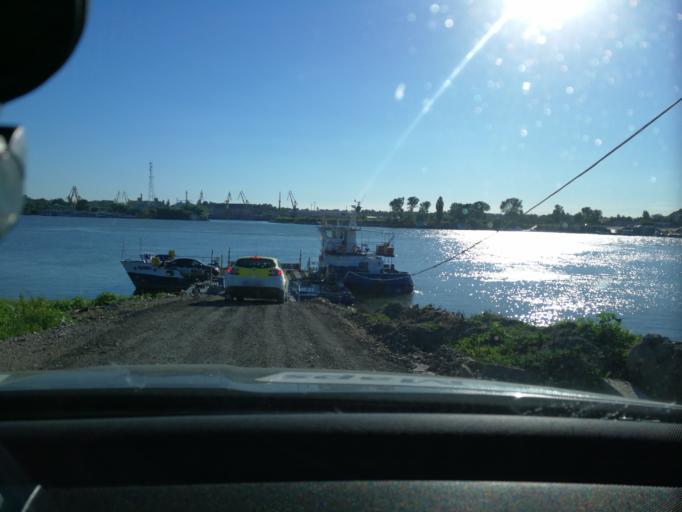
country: RO
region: Braila
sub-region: Municipiul Braila
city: Braila
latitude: 45.2869
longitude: 27.9972
